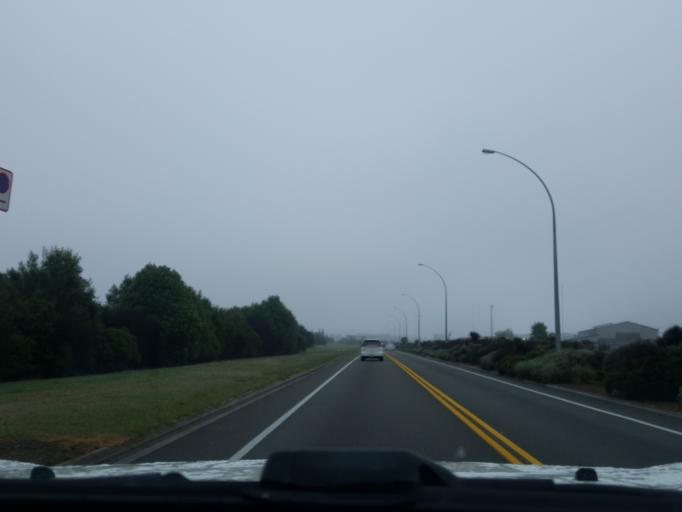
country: NZ
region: Waikato
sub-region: Hamilton City
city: Hamilton
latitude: -37.7740
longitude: 175.2454
